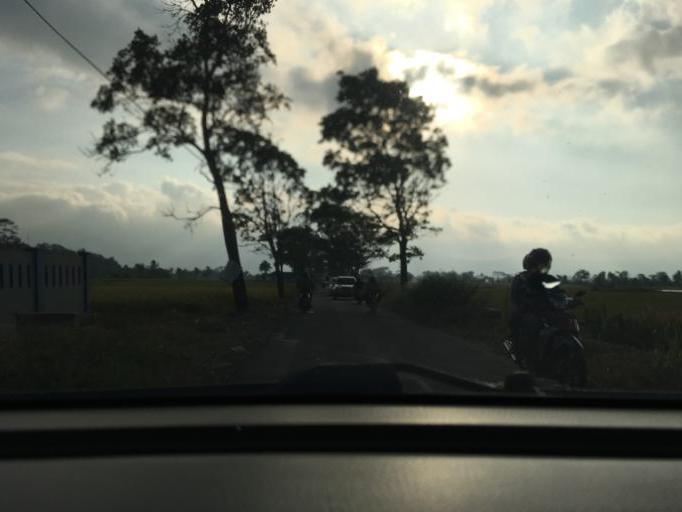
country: ID
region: West Java
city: Nagarakembang
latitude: -7.0352
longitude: 108.3345
